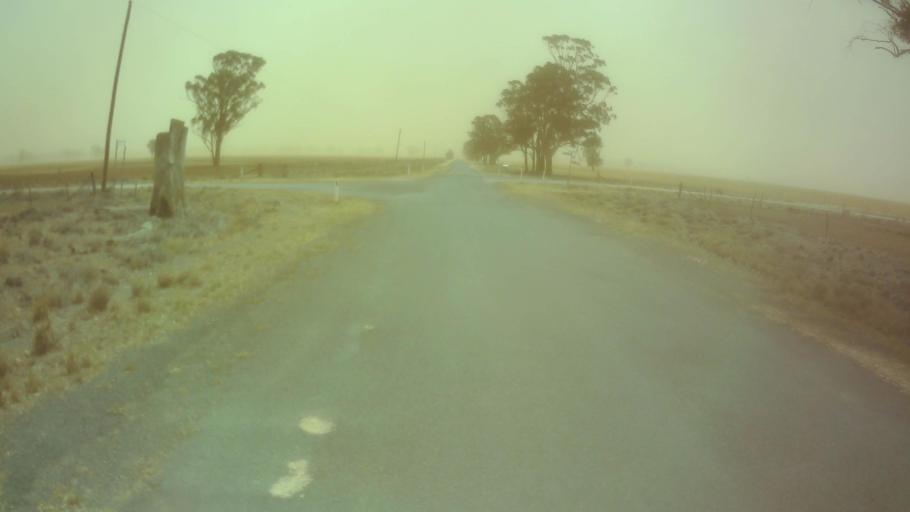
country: AU
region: New South Wales
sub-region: Weddin
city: Grenfell
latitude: -33.7041
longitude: 147.9187
